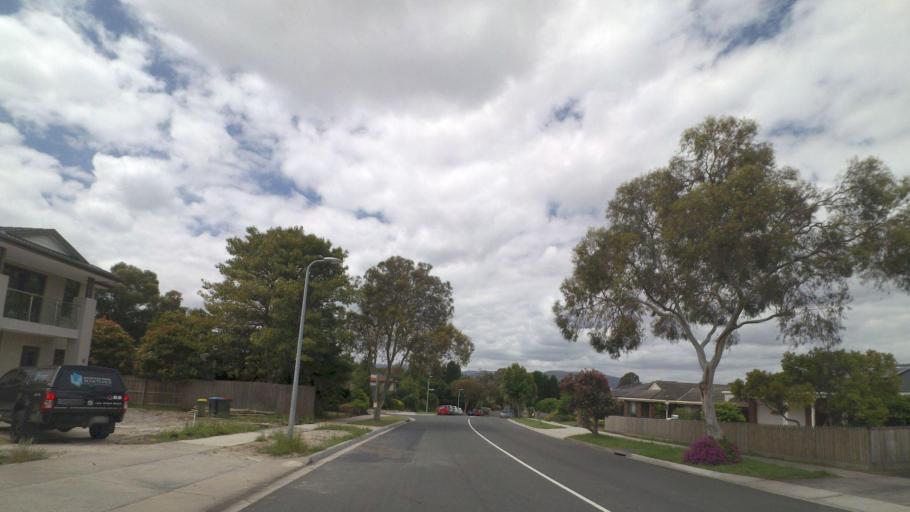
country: AU
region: Victoria
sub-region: Knox
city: Wantirna South
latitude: -37.8676
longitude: 145.2263
